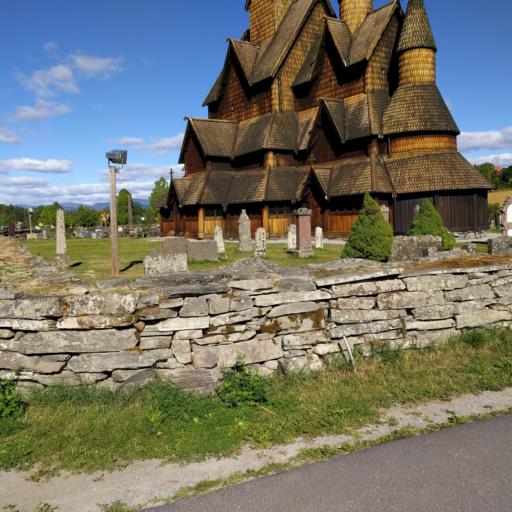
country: NO
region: Telemark
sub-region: Notodden
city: Notodden
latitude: 59.5793
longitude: 9.1768
